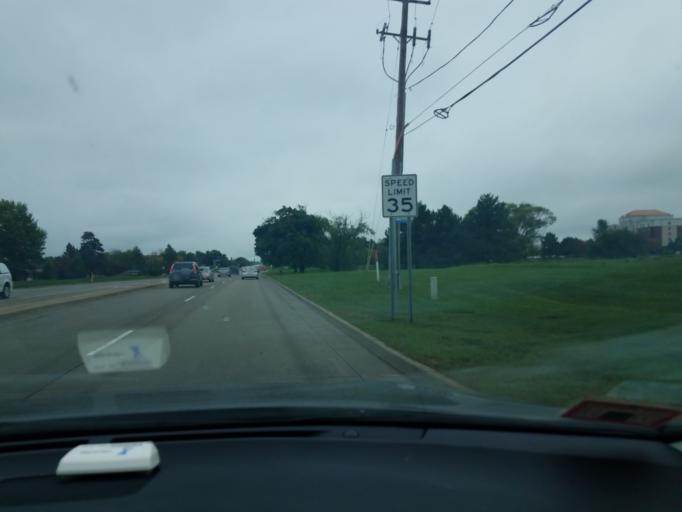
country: US
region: Illinois
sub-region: Lake County
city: Lincolnshire
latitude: 42.1972
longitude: -87.9317
